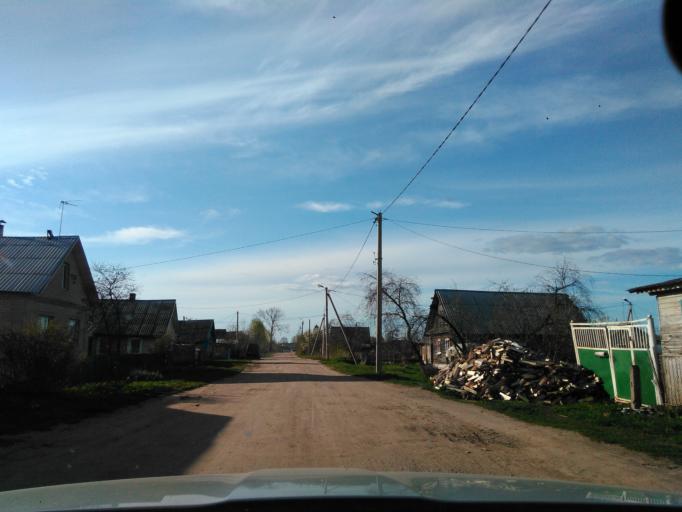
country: BY
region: Vitebsk
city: Chashniki
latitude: 54.8541
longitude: 29.1713
